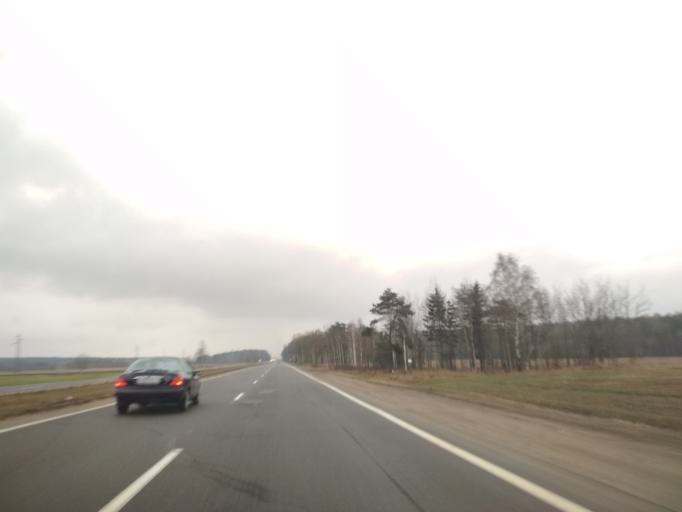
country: BY
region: Minsk
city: Dukora
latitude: 53.6306
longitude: 28.0224
